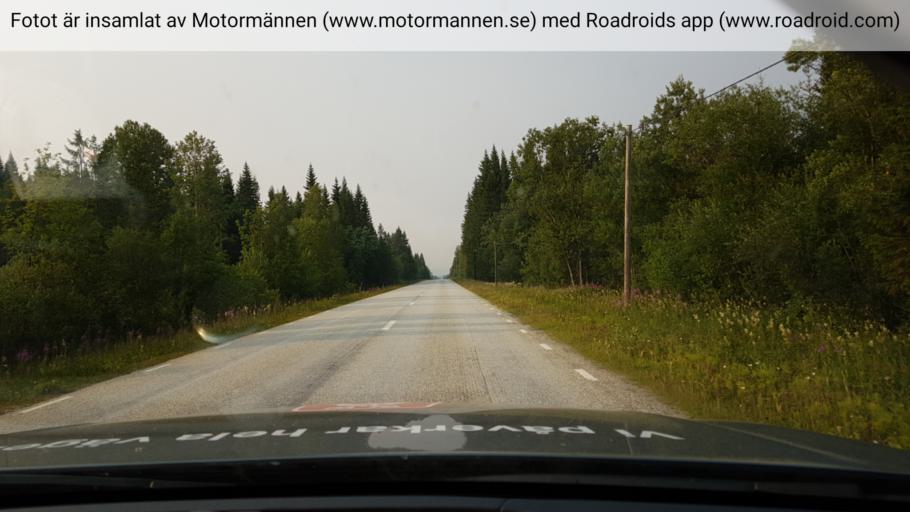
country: SE
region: Jaemtland
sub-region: Bergs Kommun
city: Hoverberg
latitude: 62.5689
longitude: 14.3049
